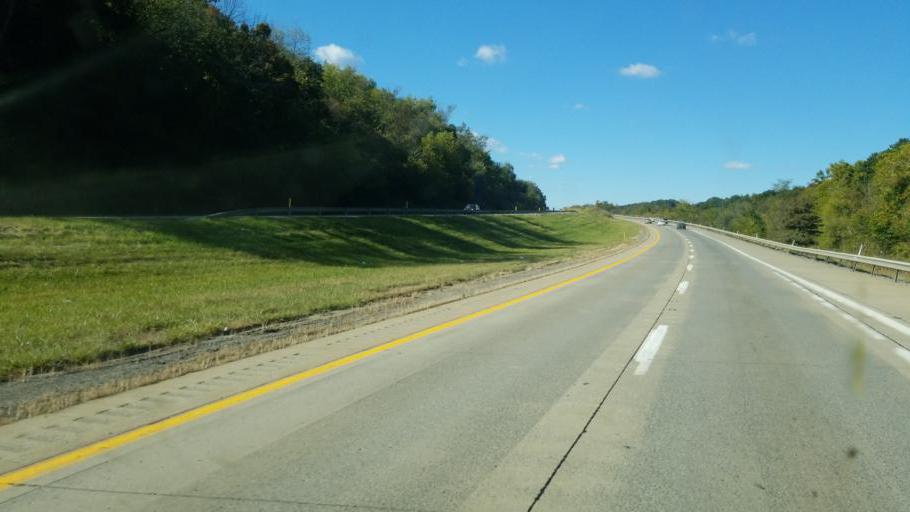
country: US
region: Pennsylvania
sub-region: Greene County
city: Waynesburg
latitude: 40.0252
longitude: -80.1742
